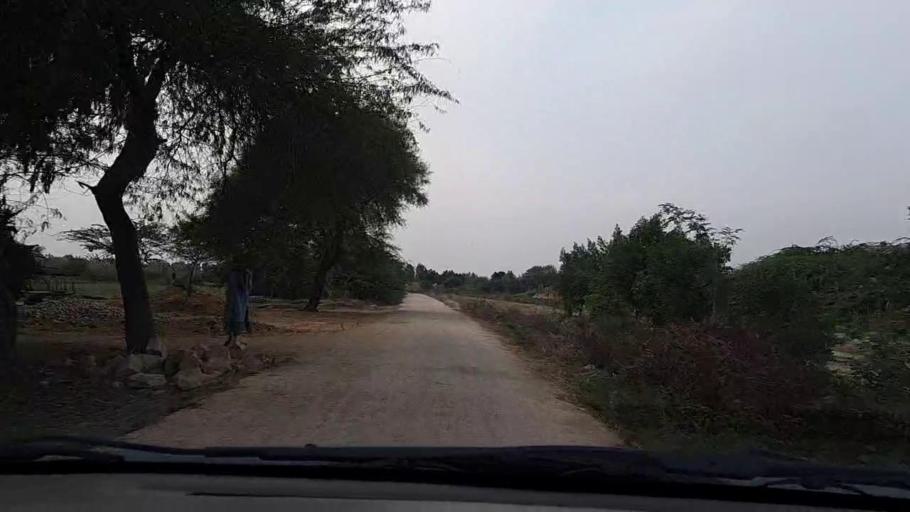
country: PK
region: Sindh
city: Thatta
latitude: 24.7698
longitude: 67.9244
